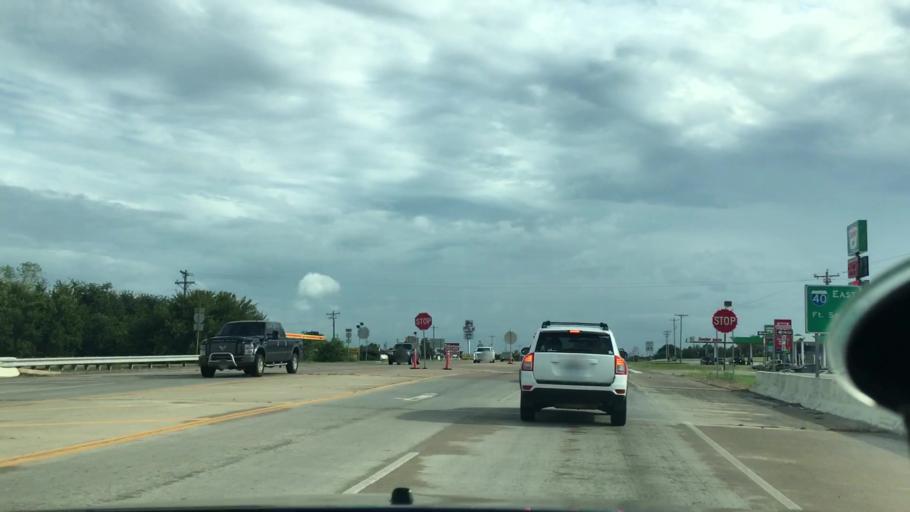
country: US
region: Oklahoma
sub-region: Lincoln County
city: Prague
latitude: 35.3835
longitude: -96.6715
